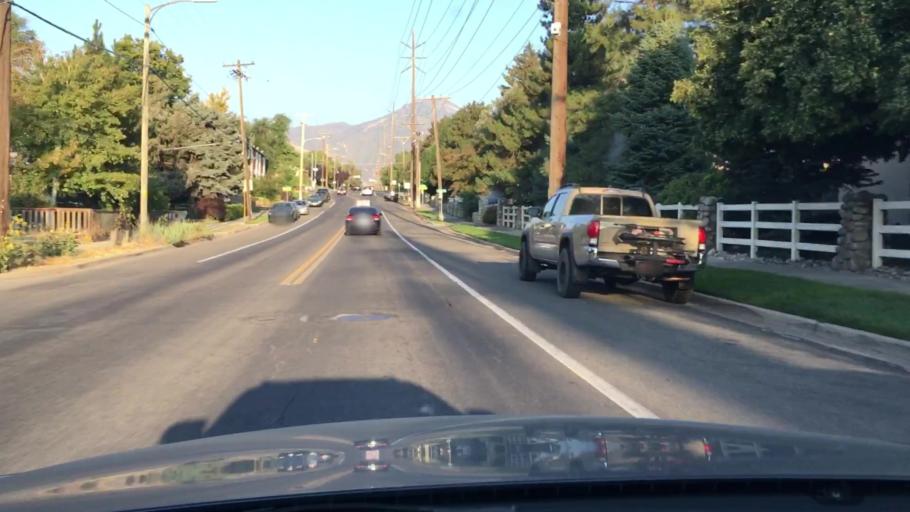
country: US
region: Utah
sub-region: Salt Lake County
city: Willard
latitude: 40.7127
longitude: -111.8580
